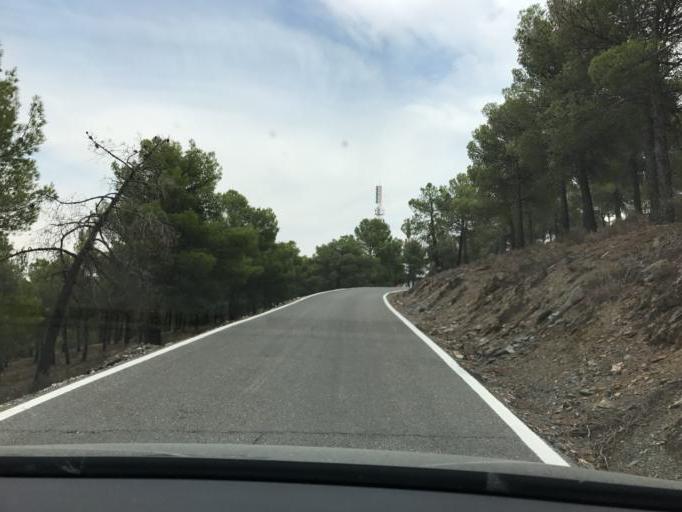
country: ES
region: Andalusia
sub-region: Provincia de Granada
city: Ferreira
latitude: 37.1691
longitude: -3.0493
